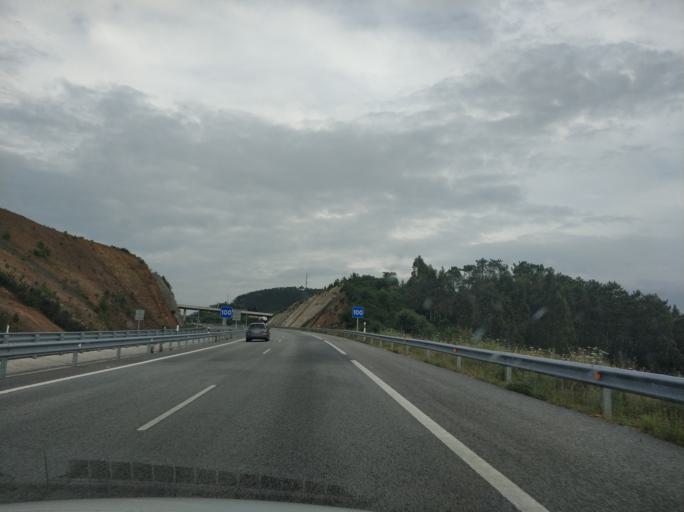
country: ES
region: Asturias
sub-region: Province of Asturias
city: Navia
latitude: 43.5384
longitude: -6.6075
